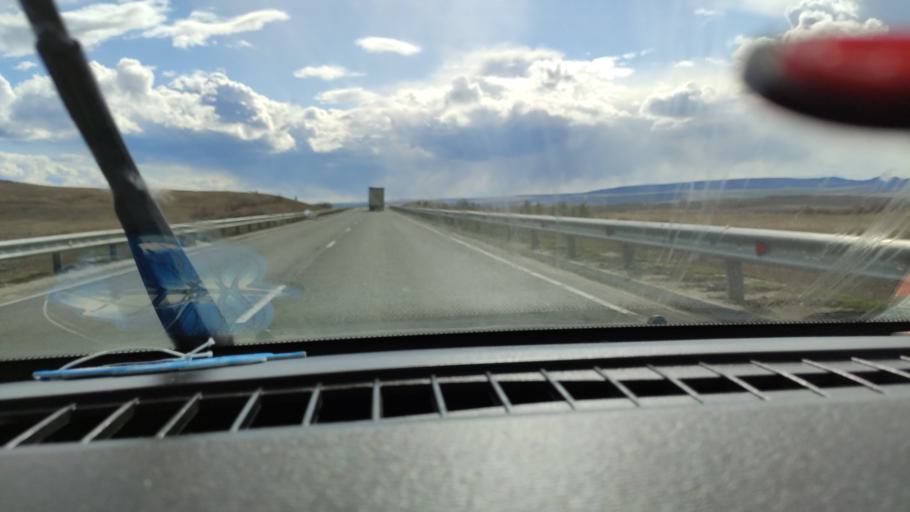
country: RU
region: Saratov
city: Alekseyevka
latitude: 52.3552
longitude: 47.9452
